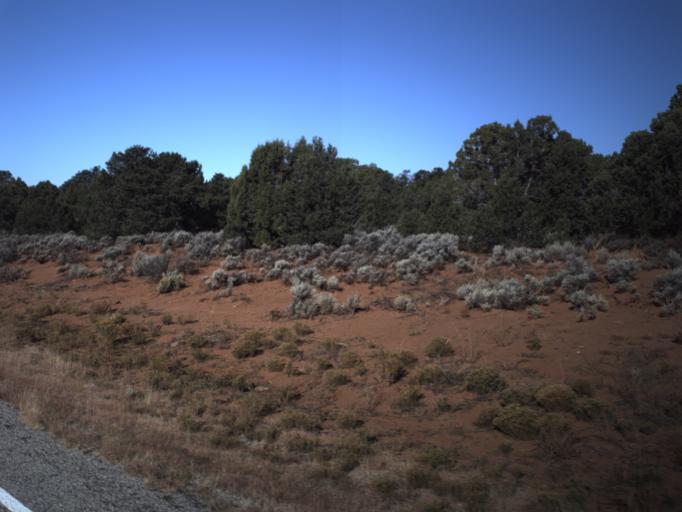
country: US
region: Utah
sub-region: San Juan County
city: Blanding
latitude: 37.5857
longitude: -109.9026
